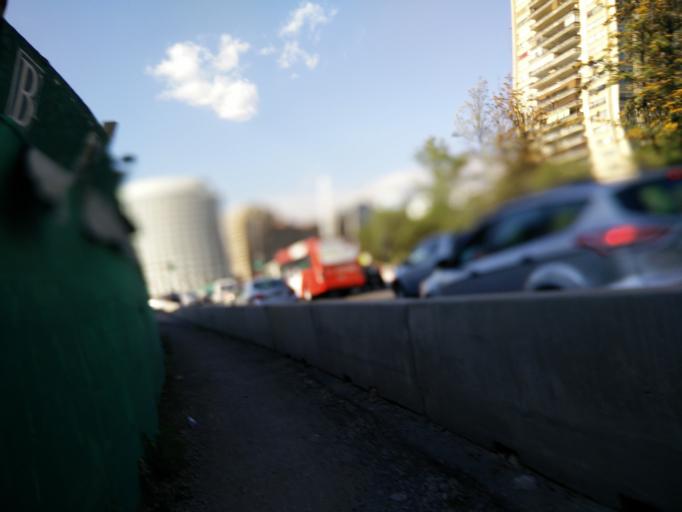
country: CL
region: Santiago Metropolitan
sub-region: Provincia de Santiago
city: Villa Presidente Frei, Nunoa, Santiago, Chile
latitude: -33.4061
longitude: -70.5863
